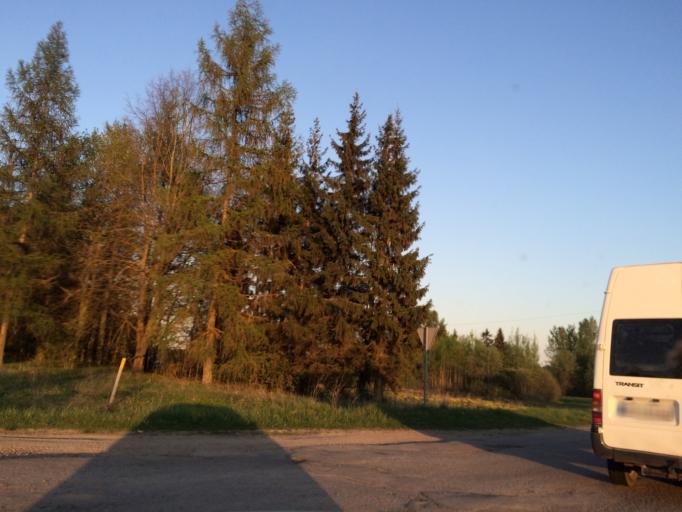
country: LV
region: Ludzas Rajons
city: Ludza
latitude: 56.5376
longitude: 27.6329
